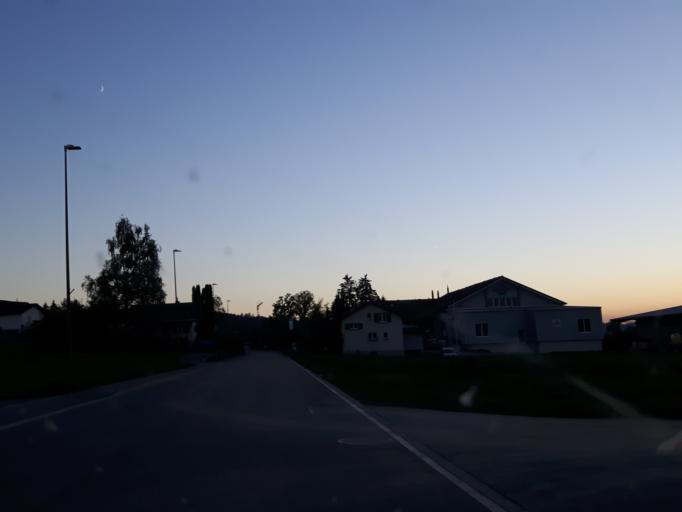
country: CH
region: Bern
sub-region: Oberaargau
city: Lotzwil
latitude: 47.1886
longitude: 7.7603
